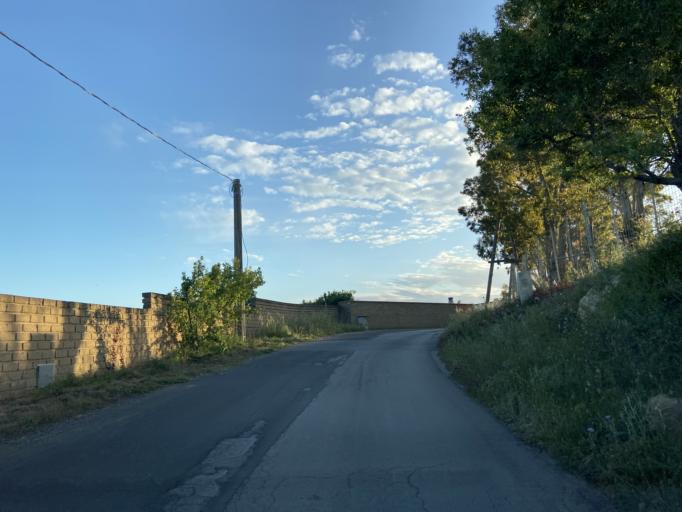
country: IT
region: Latium
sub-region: Citta metropolitana di Roma Capitale
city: Civitavecchia
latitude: 42.0796
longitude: 11.8399
